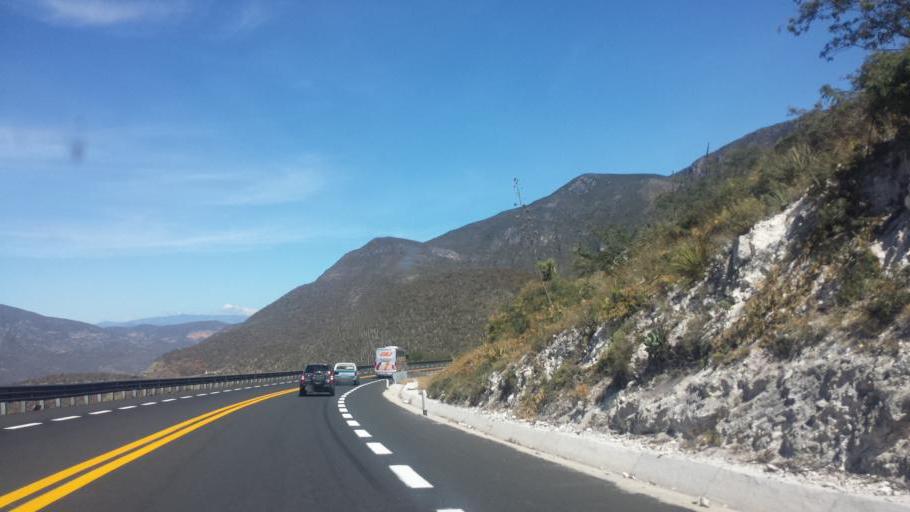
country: MX
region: Puebla
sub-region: San Jose Miahuatlan
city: San Pedro Tetitlan
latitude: 18.0867
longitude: -97.3503
